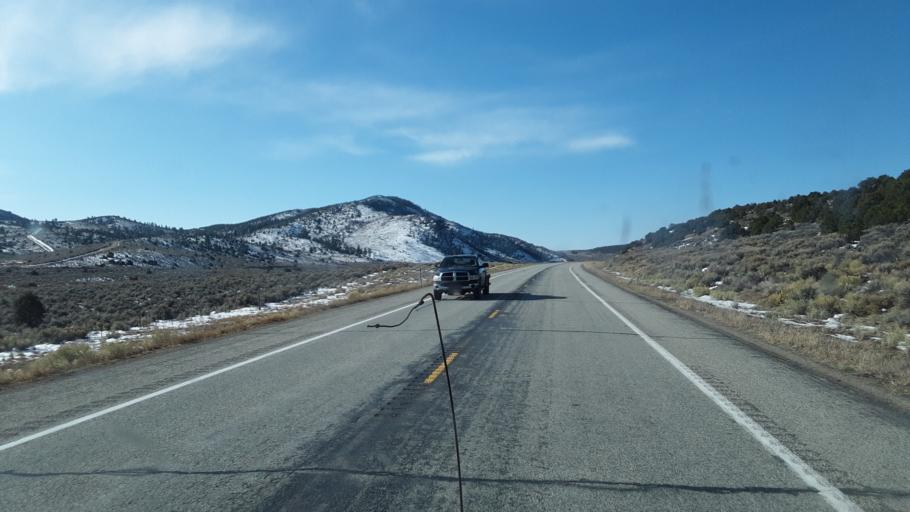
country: US
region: Colorado
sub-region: Costilla County
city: San Luis
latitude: 37.5094
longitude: -105.3172
